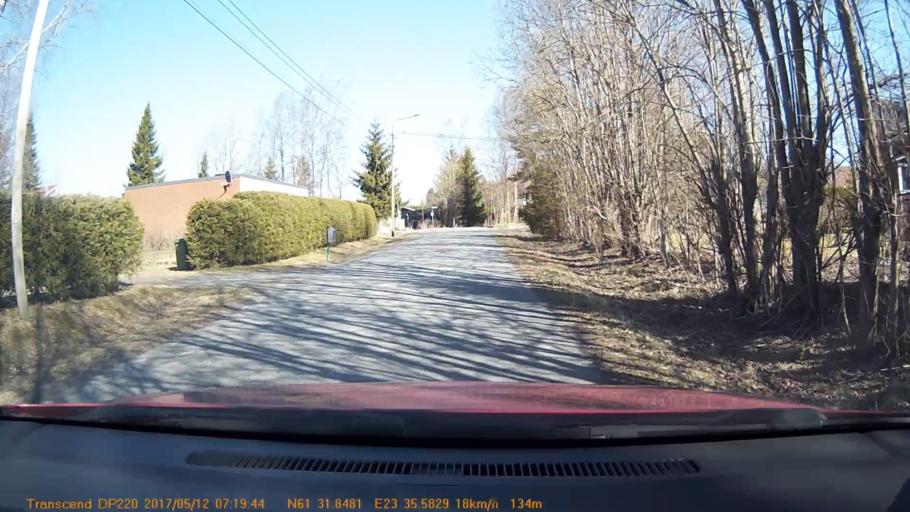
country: FI
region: Pirkanmaa
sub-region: Tampere
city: Yloejaervi
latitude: 61.5308
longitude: 23.5930
